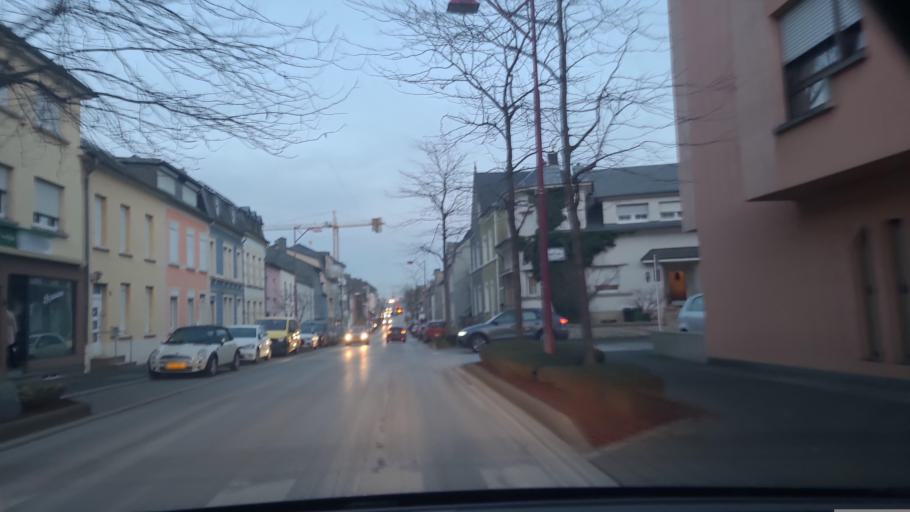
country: LU
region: Luxembourg
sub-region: Canton d'Esch-sur-Alzette
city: Petange
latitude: 49.5575
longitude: 5.8830
